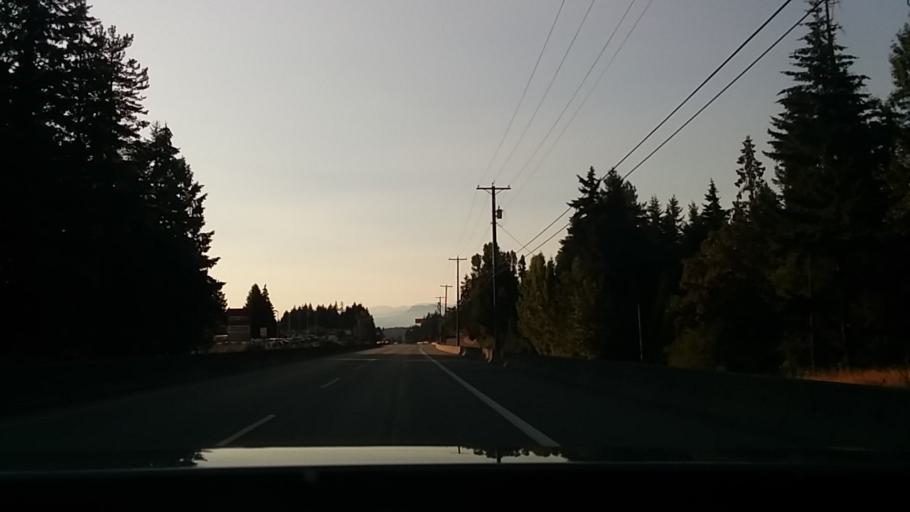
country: CA
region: British Columbia
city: Duncan
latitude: 48.6933
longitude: -123.5878
